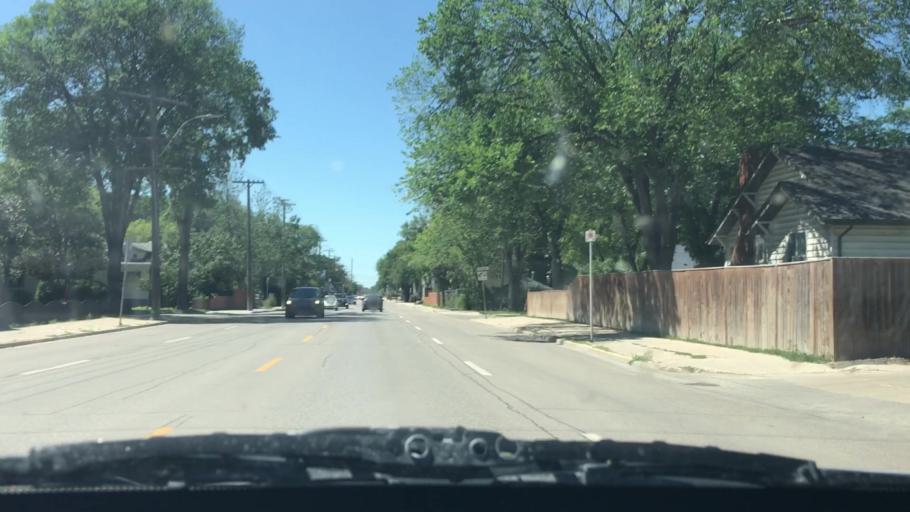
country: CA
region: Manitoba
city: Winnipeg
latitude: 49.8740
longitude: -97.1882
